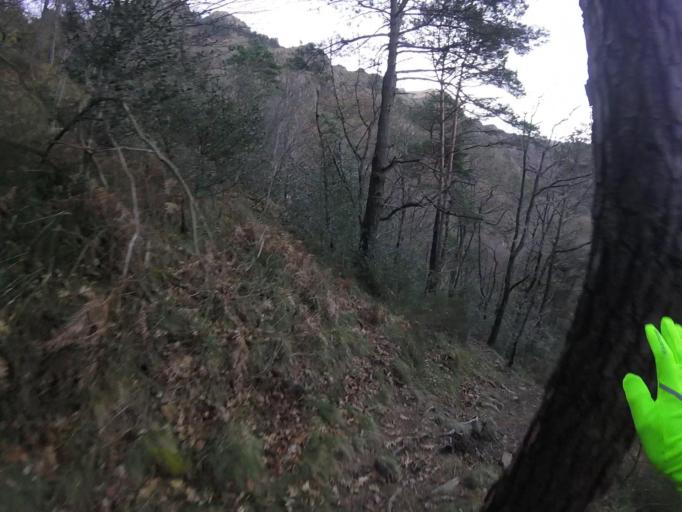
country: ES
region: Basque Country
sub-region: Provincia de Guipuzcoa
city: Irun
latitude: 43.2891
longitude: -1.7919
